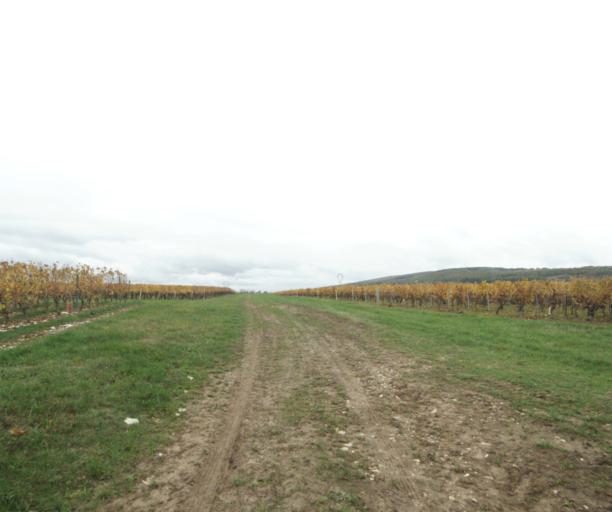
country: FR
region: Rhone-Alpes
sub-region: Departement de l'Ain
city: Pont-de-Vaux
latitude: 46.4723
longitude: 4.8621
